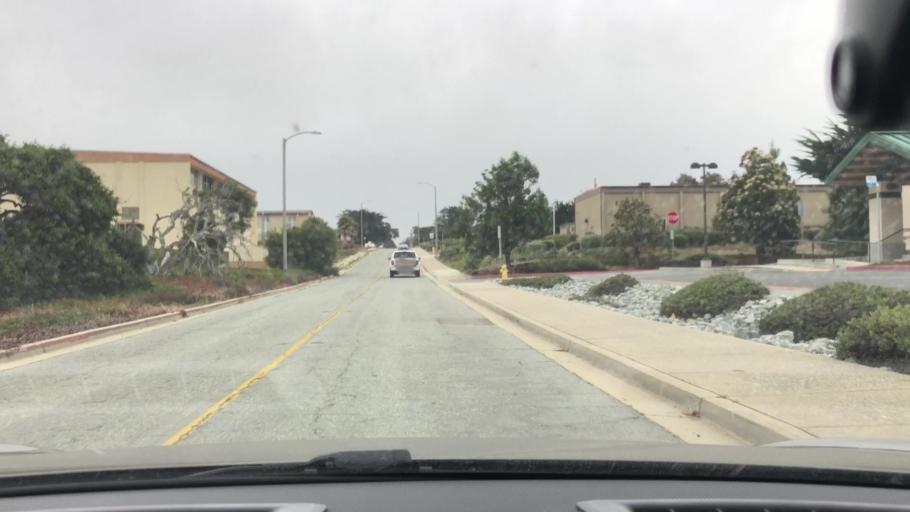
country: US
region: California
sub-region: Monterey County
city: Marina
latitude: 36.6464
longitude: -121.8017
